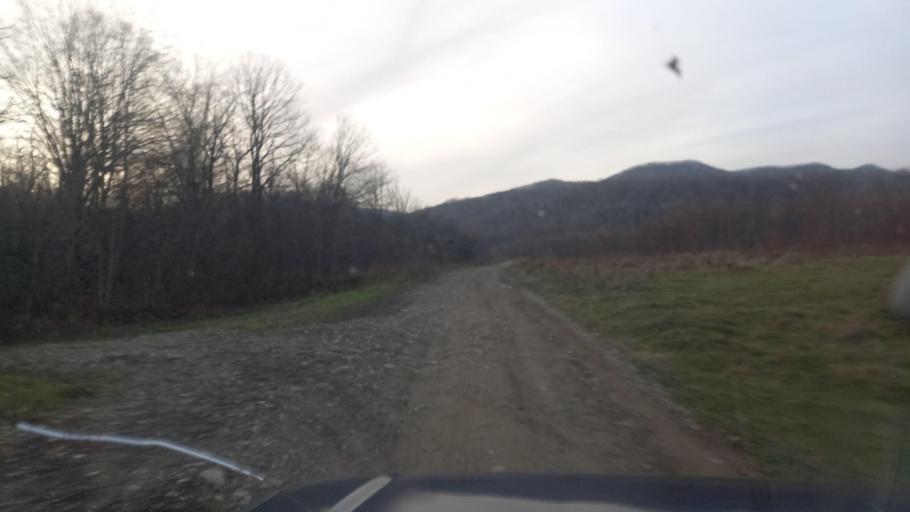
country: RU
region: Krasnodarskiy
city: Goryachiy Klyuch
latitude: 44.3813
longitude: 39.1566
